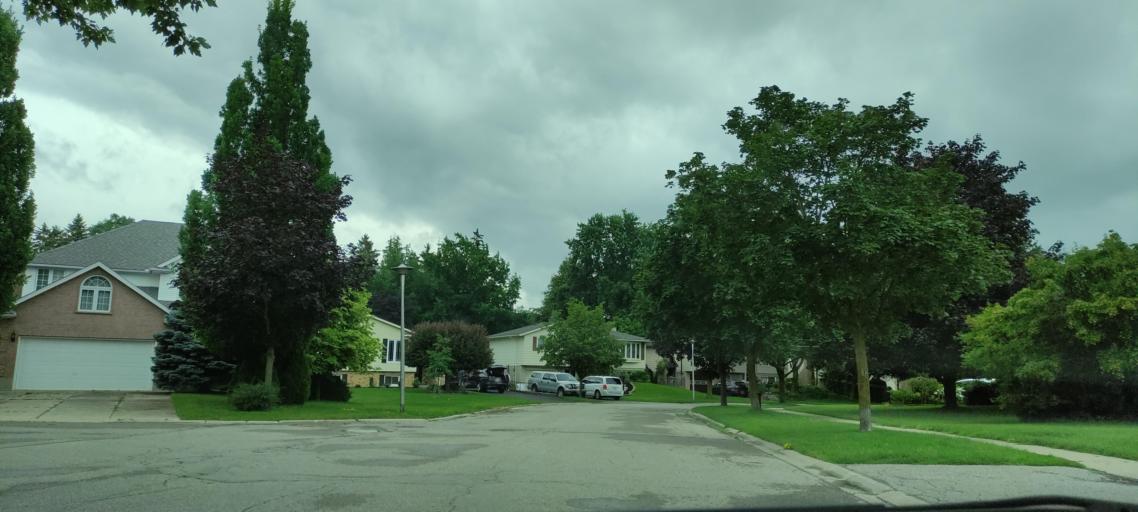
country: CA
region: Ontario
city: Stratford
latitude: 43.3829
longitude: -80.9748
